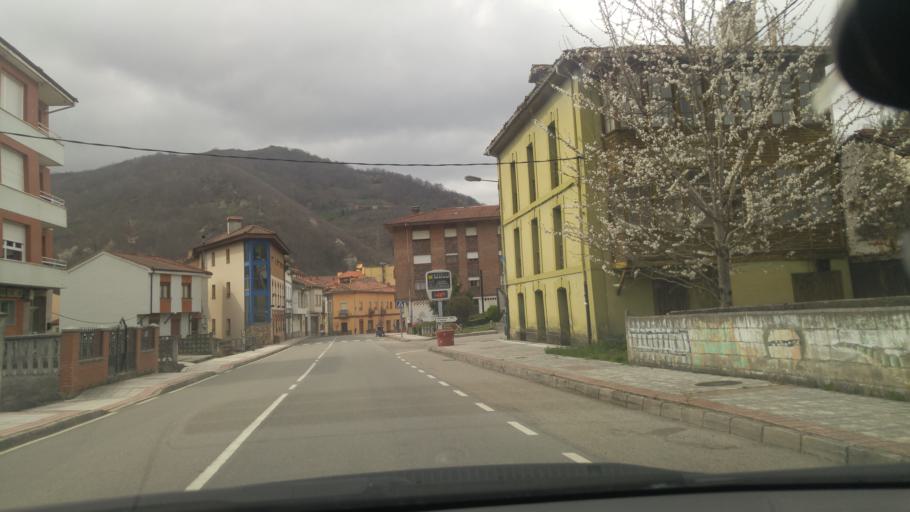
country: ES
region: Asturias
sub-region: Province of Asturias
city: Rio Aller
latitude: 43.1230
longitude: -5.5623
